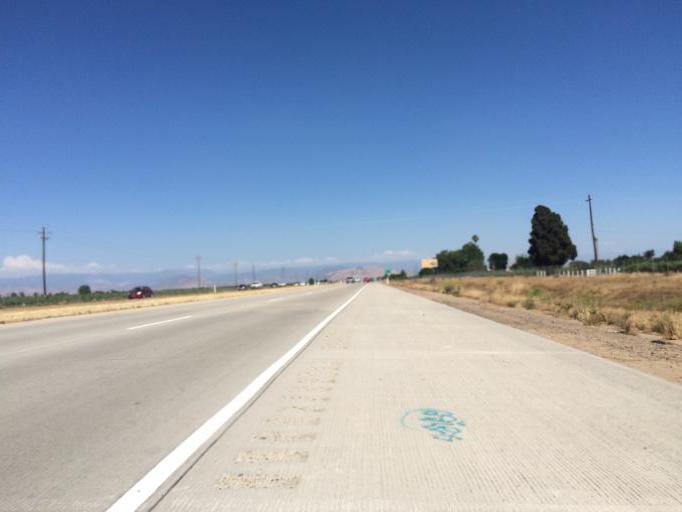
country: US
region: California
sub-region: Fresno County
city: Sanger
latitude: 36.7359
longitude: -119.6235
